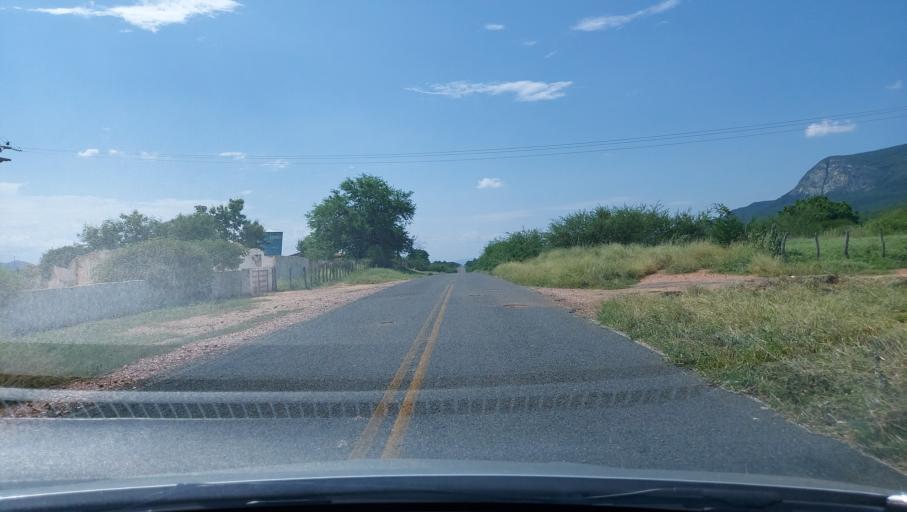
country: BR
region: Bahia
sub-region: Oliveira Dos Brejinhos
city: Beira Rio
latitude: -12.1471
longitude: -42.5551
